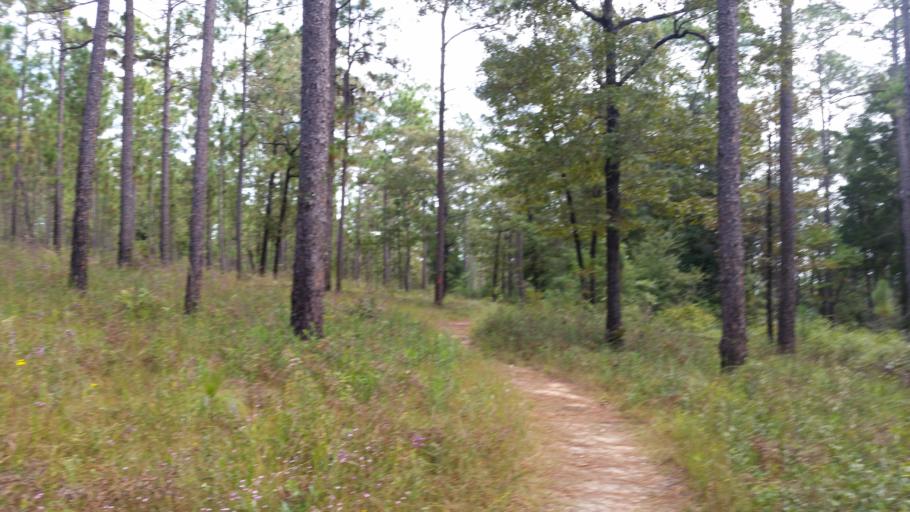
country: US
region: Florida
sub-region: Santa Rosa County
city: Point Baker
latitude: 30.8618
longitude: -86.8423
